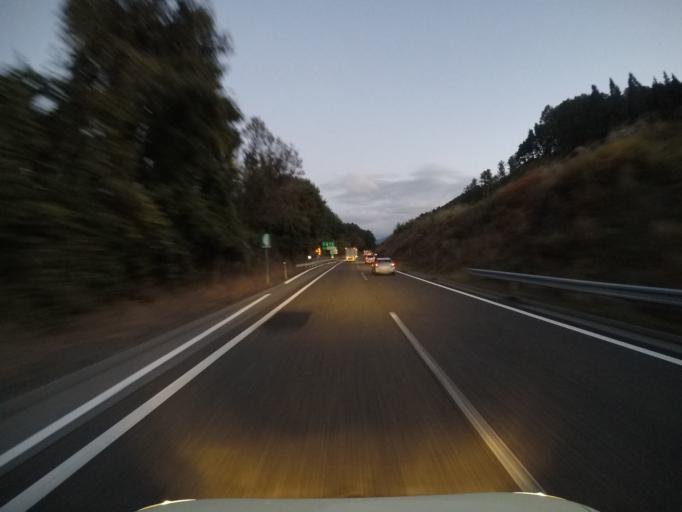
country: JP
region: Nagano
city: Okaya
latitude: 36.0416
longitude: 138.0594
